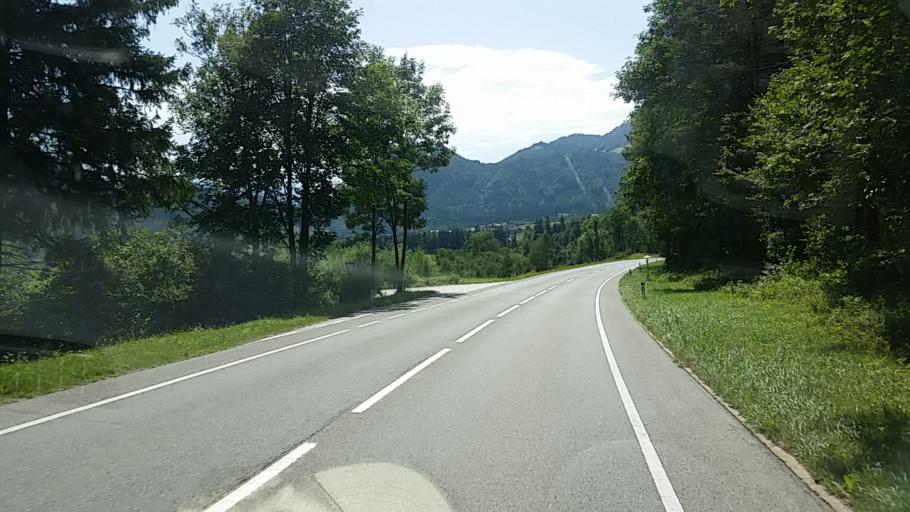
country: AT
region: Salzburg
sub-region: Politischer Bezirk Sankt Johann im Pongau
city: Werfen
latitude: 47.5108
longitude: 13.1670
